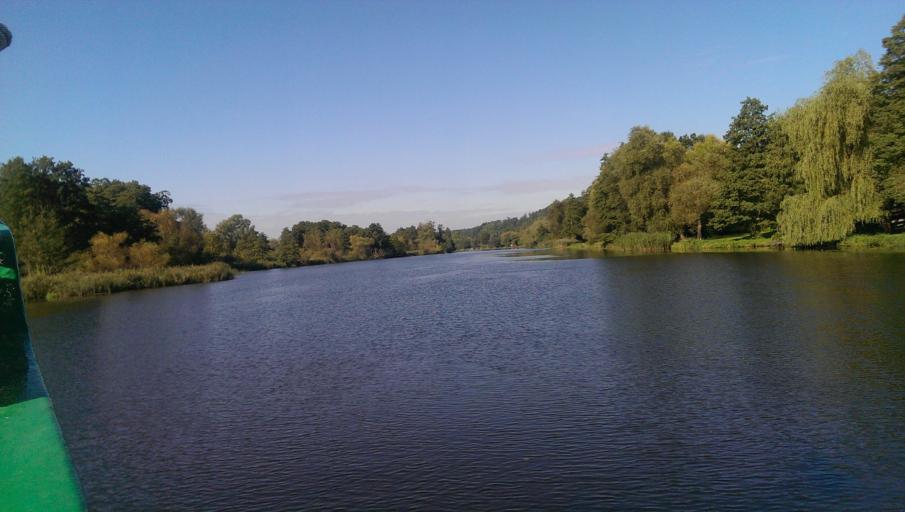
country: DE
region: Brandenburg
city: Liepe
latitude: 52.8601
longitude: 14.0053
